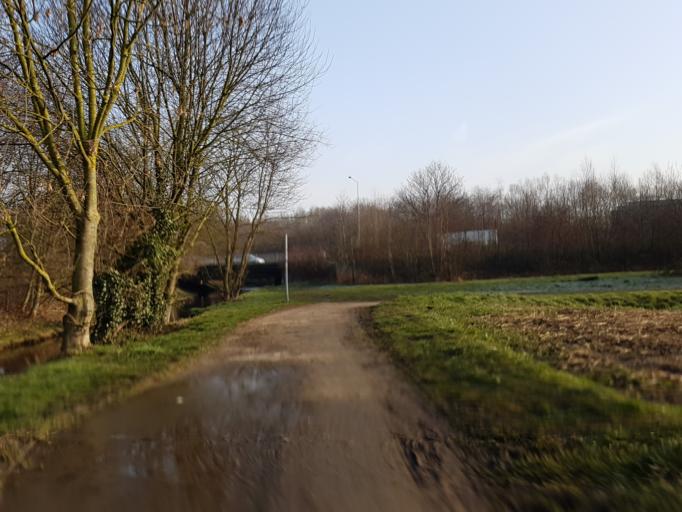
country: DE
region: North Rhine-Westphalia
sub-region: Regierungsbezirk Koln
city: Wurselen
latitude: 50.7888
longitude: 6.1197
